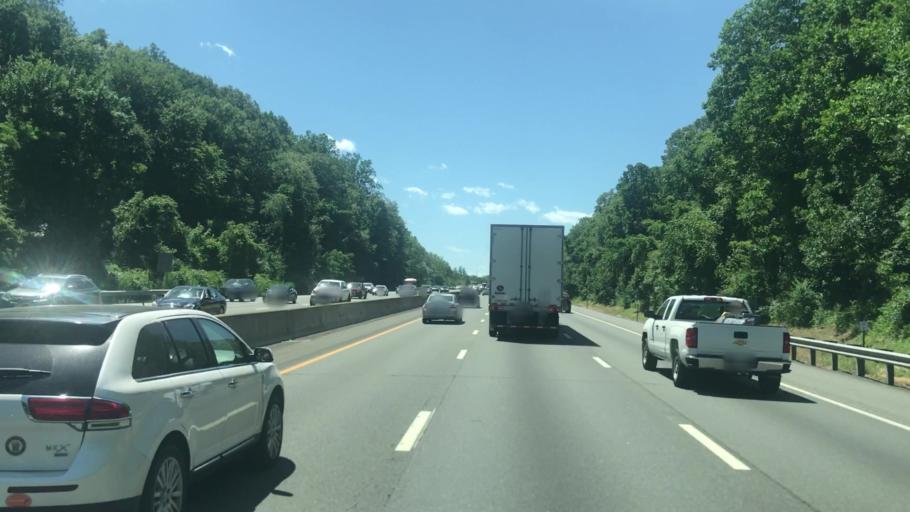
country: US
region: New York
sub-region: Rockland County
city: West Nyack
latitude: 41.1012
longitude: -73.9787
